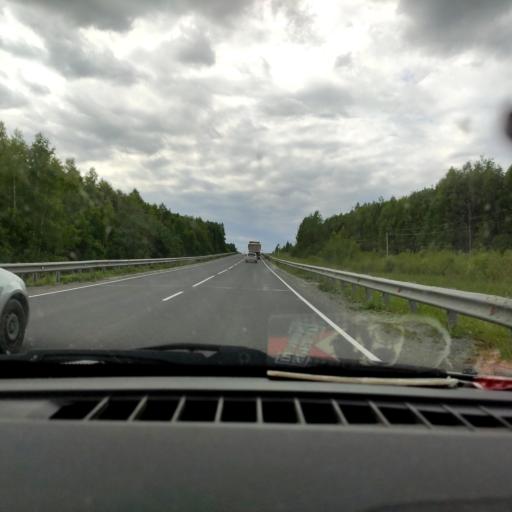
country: RU
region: Perm
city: Verkhnechusovskiye Gorodki
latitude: 58.2337
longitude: 57.0865
